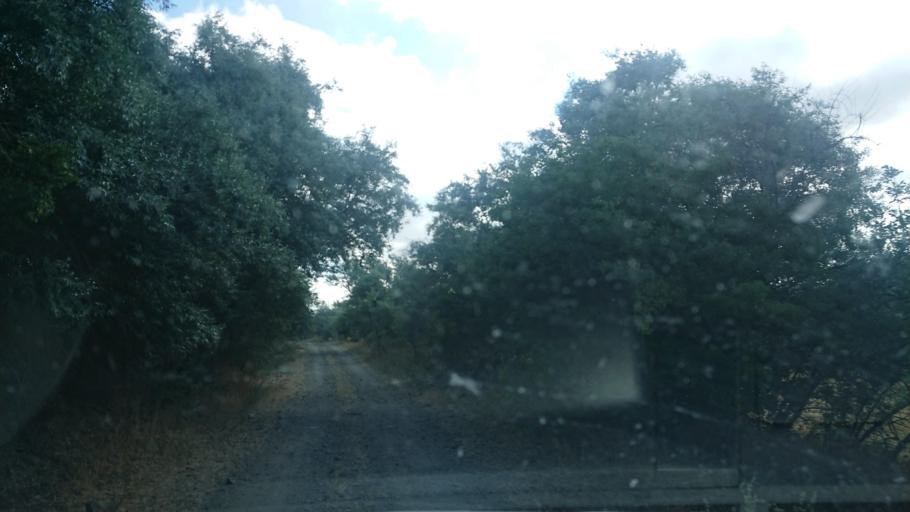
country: TR
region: Aksaray
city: Agacoren
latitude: 38.8583
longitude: 33.9372
